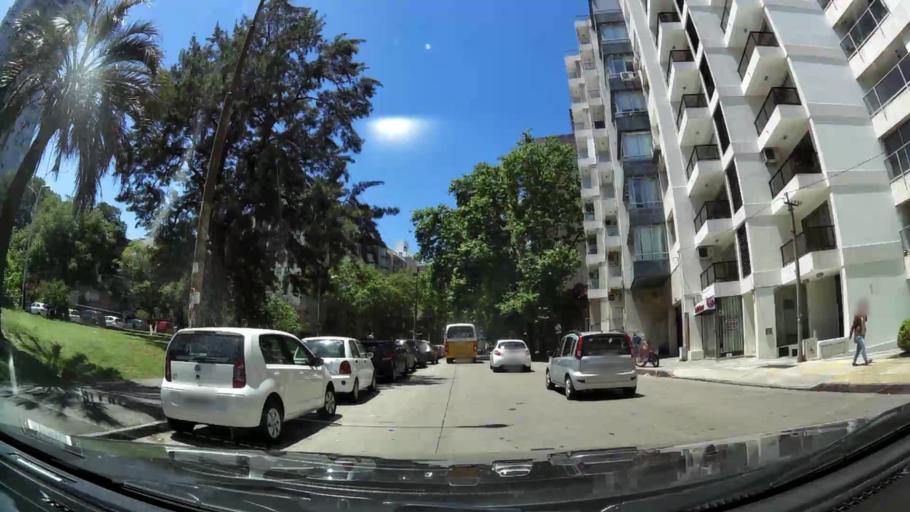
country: UY
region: Montevideo
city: Montevideo
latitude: -34.9066
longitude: -56.1628
